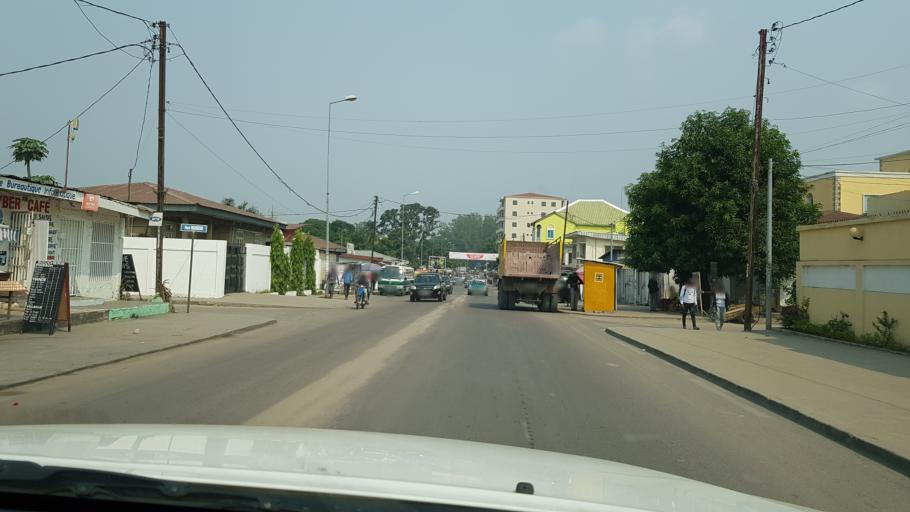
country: CG
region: Brazzaville
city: Brazzaville
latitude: -4.2605
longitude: 15.2604
